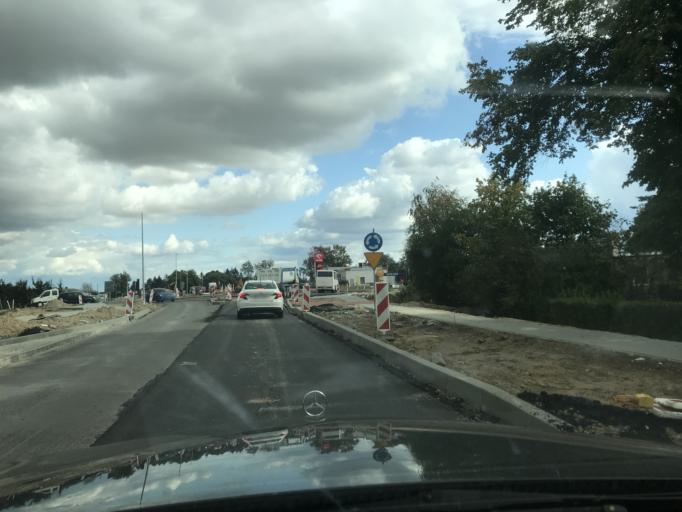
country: PL
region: Lublin Voivodeship
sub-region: Powiat lubartowski
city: Lubartow
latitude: 51.4747
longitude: 22.6037
